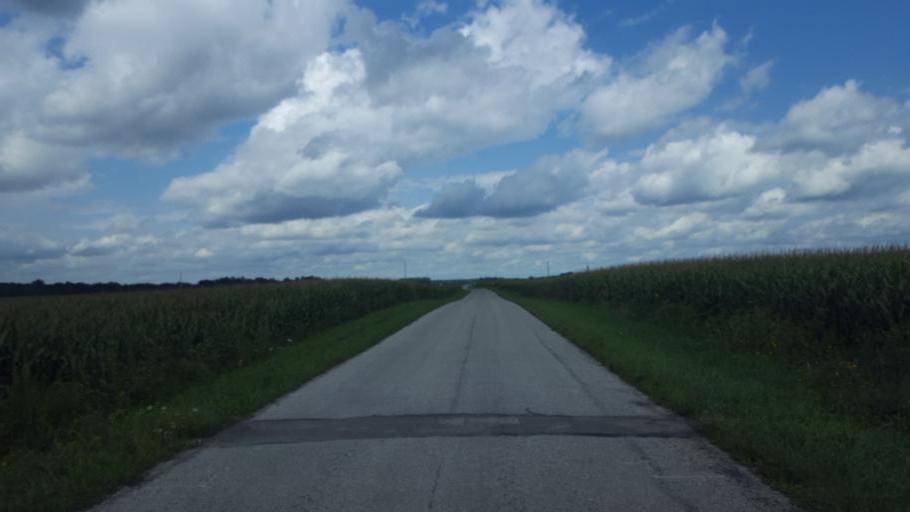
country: US
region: Ohio
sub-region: Huron County
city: Willard
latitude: 41.1403
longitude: -82.7559
